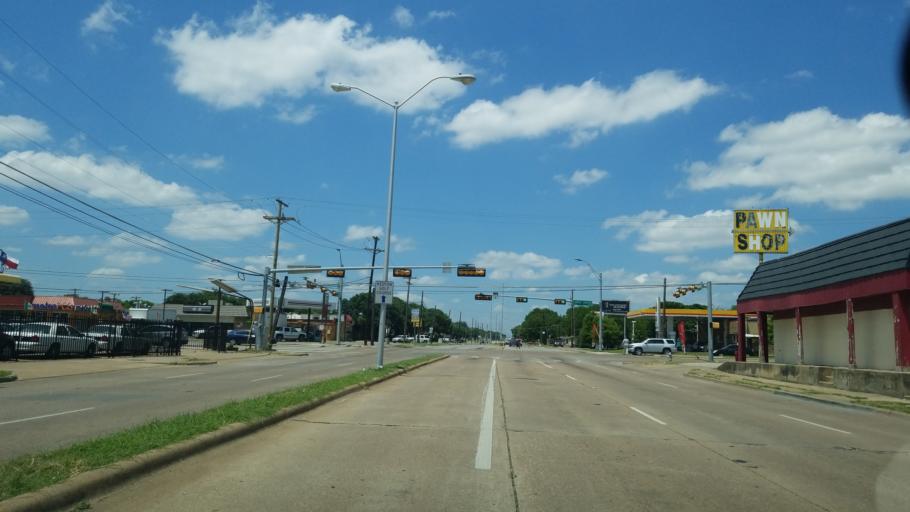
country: US
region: Texas
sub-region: Dallas County
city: Balch Springs
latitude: 32.7338
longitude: -96.7001
